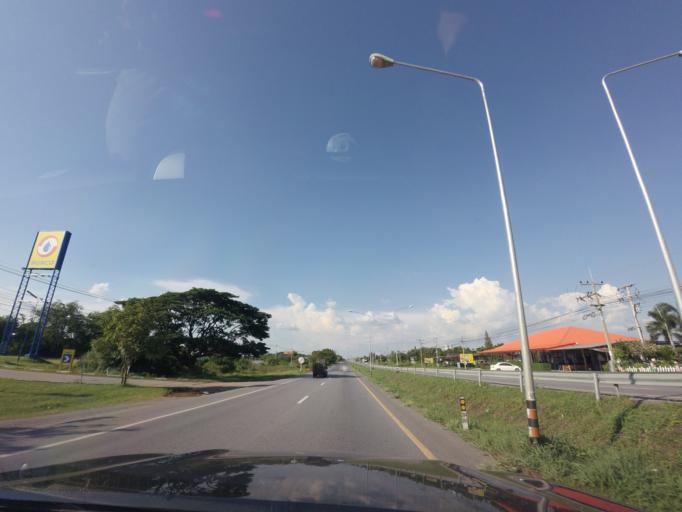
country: TH
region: Khon Kaen
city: Non Sila
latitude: 15.9795
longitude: 102.6954
